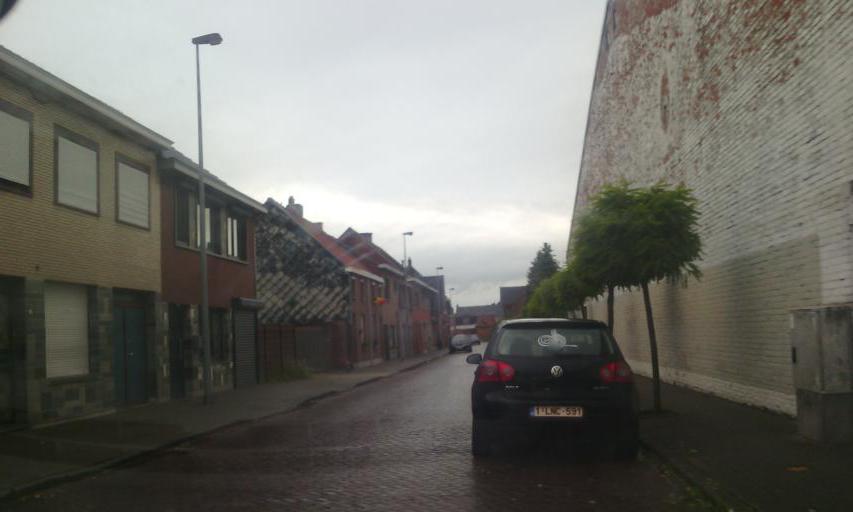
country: BE
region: Flanders
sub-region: Provincie Oost-Vlaanderen
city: Zele
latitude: 51.0677
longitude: 4.0295
